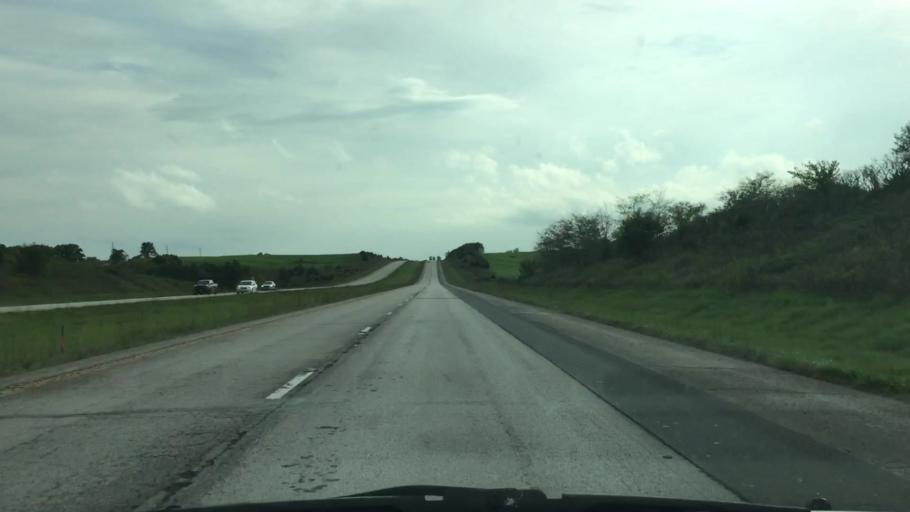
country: US
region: Iowa
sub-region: Decatur County
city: Lamoni
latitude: 40.5063
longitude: -93.9659
